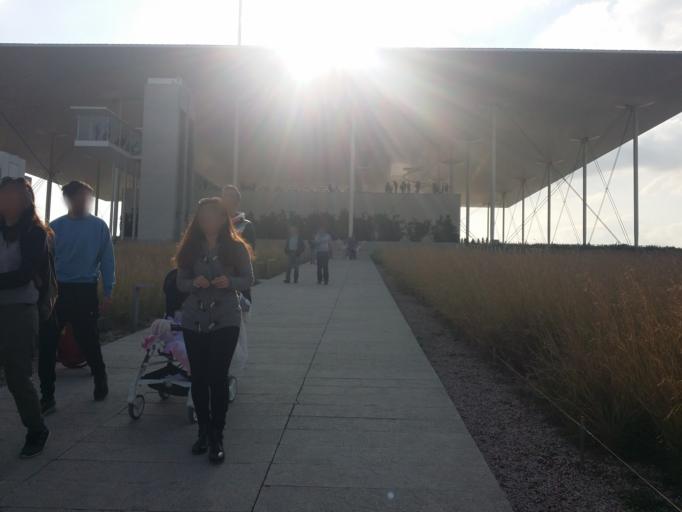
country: GR
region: Attica
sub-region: Nomarchia Athinas
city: Kallithea
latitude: 37.9403
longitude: 23.6921
